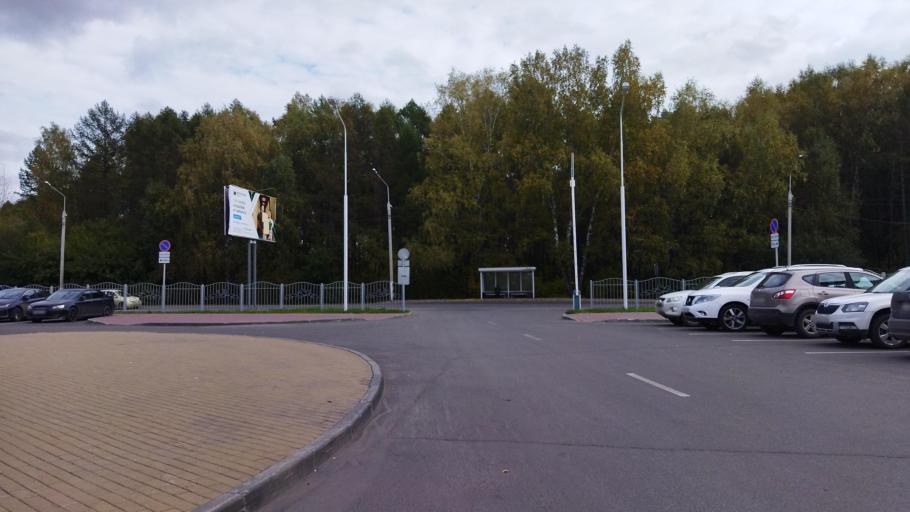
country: RU
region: Tomsk
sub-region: Tomskiy Rayon
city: Tomsk
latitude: 56.4933
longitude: 85.0586
